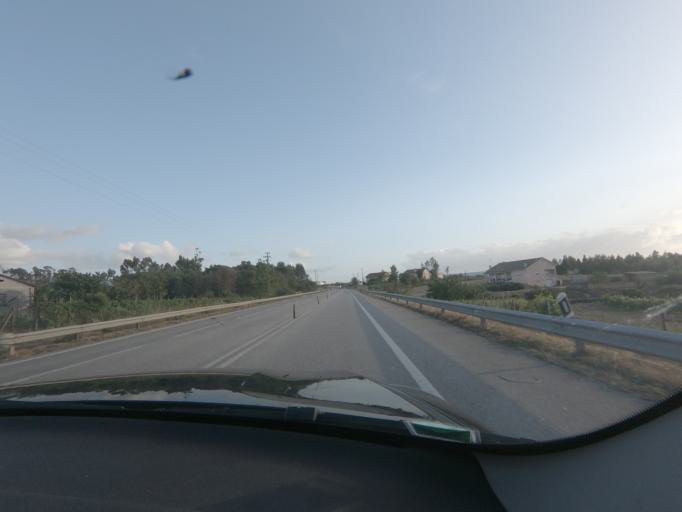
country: PT
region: Viseu
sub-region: Santa Comba Dao
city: Santa Comba Dao
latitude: 40.3655
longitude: -8.1322
